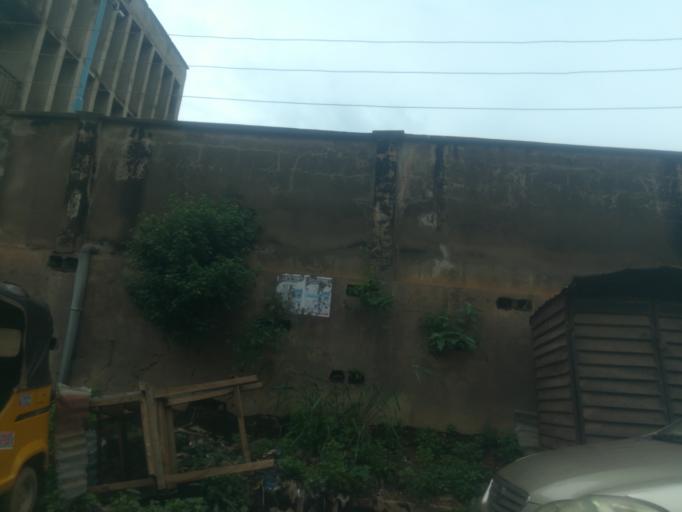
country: NG
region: Oyo
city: Ibadan
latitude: 7.3396
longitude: 3.9068
